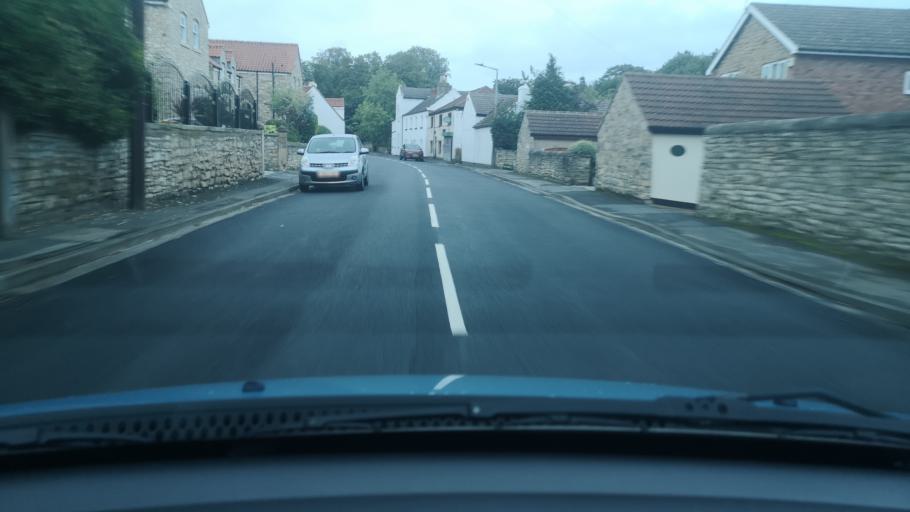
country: GB
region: England
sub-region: Doncaster
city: Campsall
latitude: 53.6189
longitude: -1.1812
